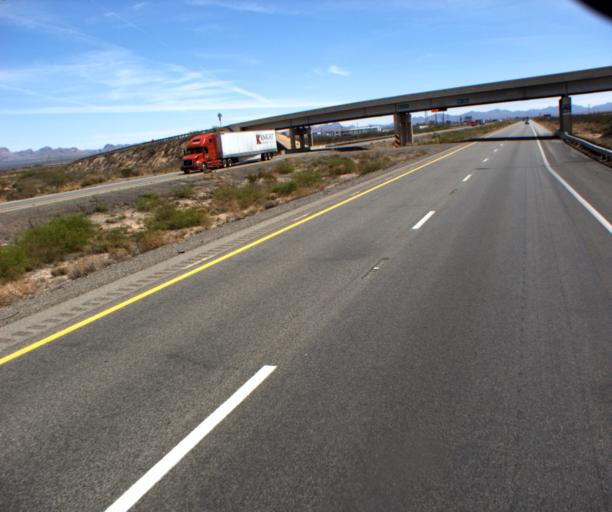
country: US
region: New Mexico
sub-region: Hidalgo County
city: Lordsburg
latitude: 32.2721
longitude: -109.2506
